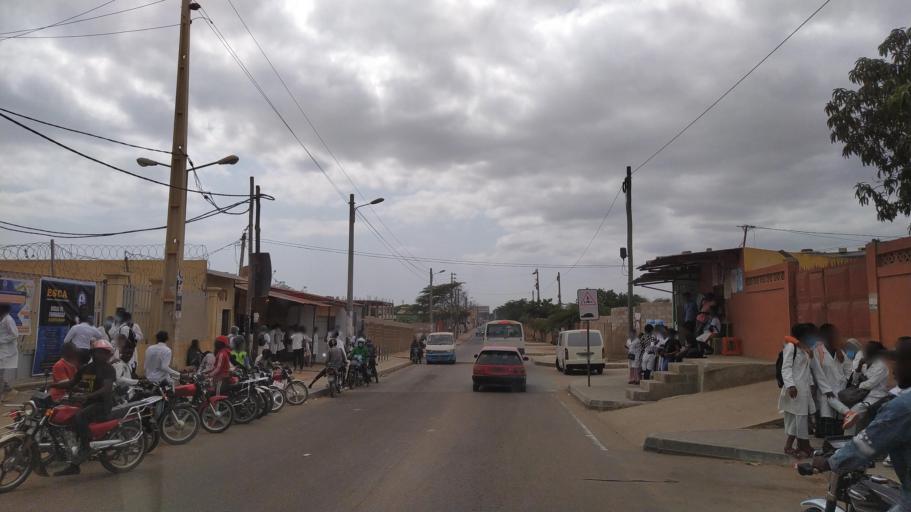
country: AO
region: Luanda
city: Luanda
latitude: -8.9731
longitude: 13.1498
